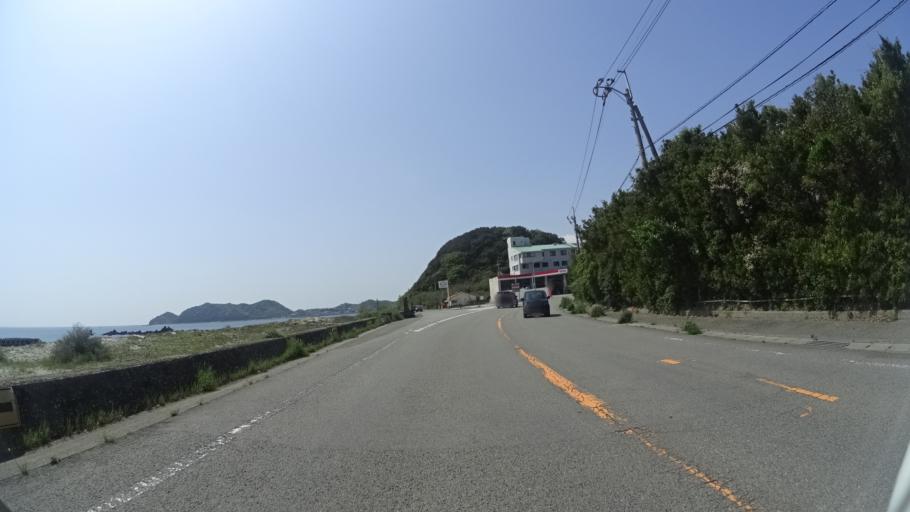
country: JP
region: Tokushima
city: Narutocho-mitsuishi
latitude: 34.1967
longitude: 134.6255
